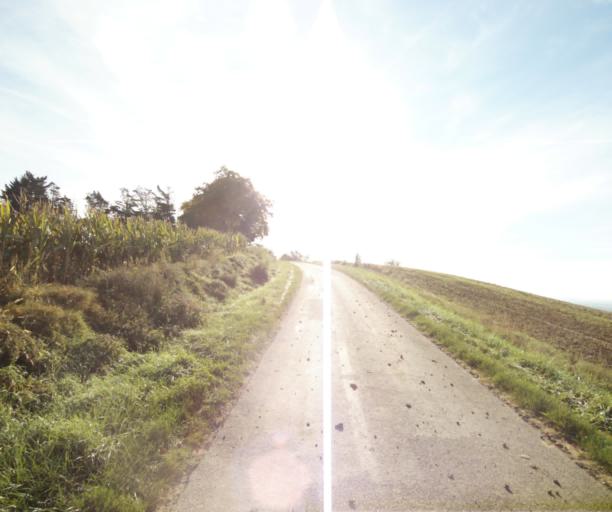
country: FR
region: Midi-Pyrenees
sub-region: Departement du Tarn-et-Garonne
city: Nohic
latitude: 43.9171
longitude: 1.4531
